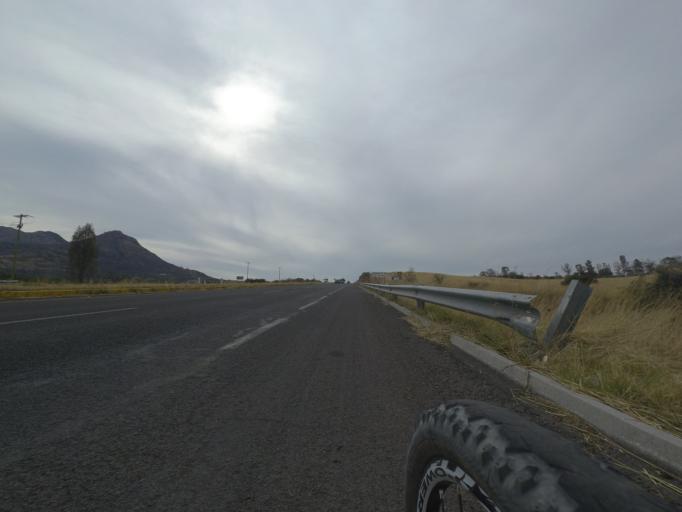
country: MX
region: Aguascalientes
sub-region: Aguascalientes
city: La Loma de los Negritos
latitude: 21.8916
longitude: -102.4002
